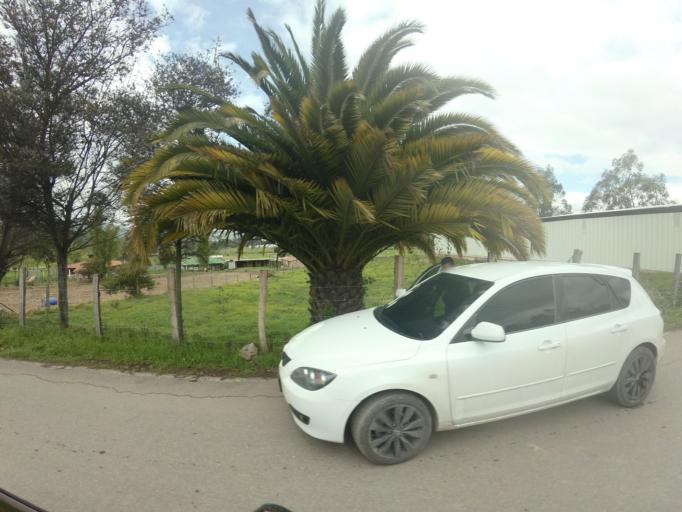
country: CO
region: Boyaca
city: Nobsa
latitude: 5.7862
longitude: -72.9719
